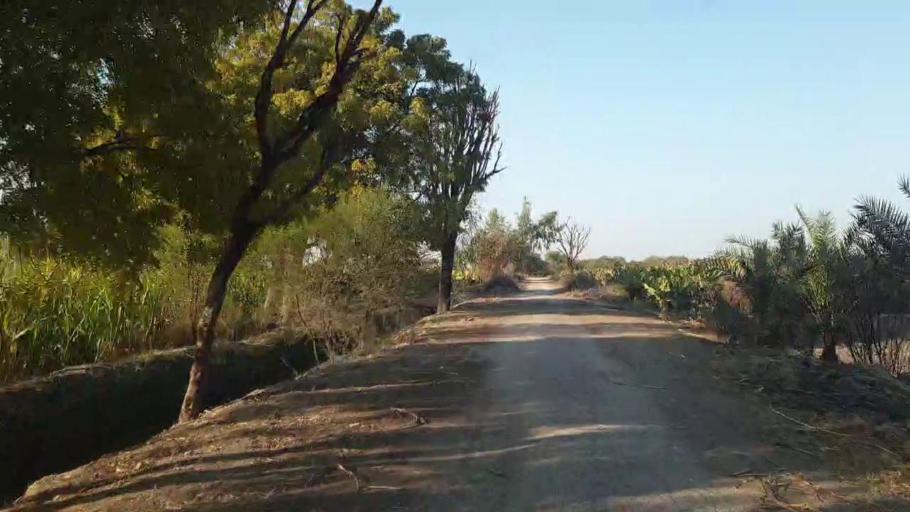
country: PK
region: Sindh
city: Tando Allahyar
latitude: 25.3754
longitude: 68.7014
